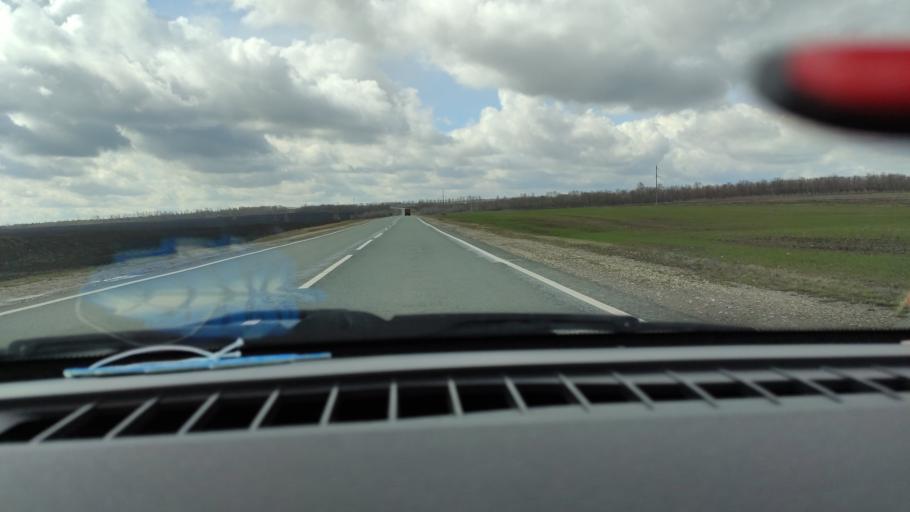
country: RU
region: Samara
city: Yelkhovka
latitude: 53.8836
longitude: 50.2624
